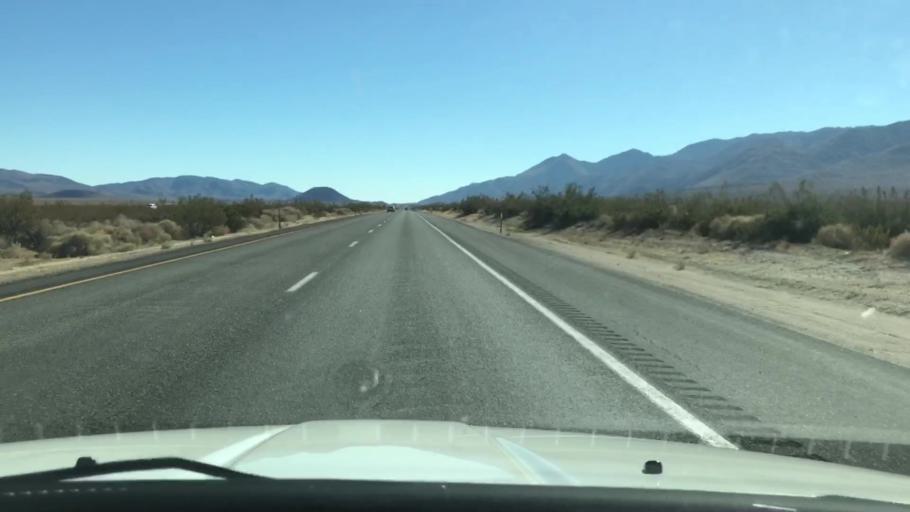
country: US
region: California
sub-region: Kern County
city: Inyokern
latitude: 36.0737
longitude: -117.9569
